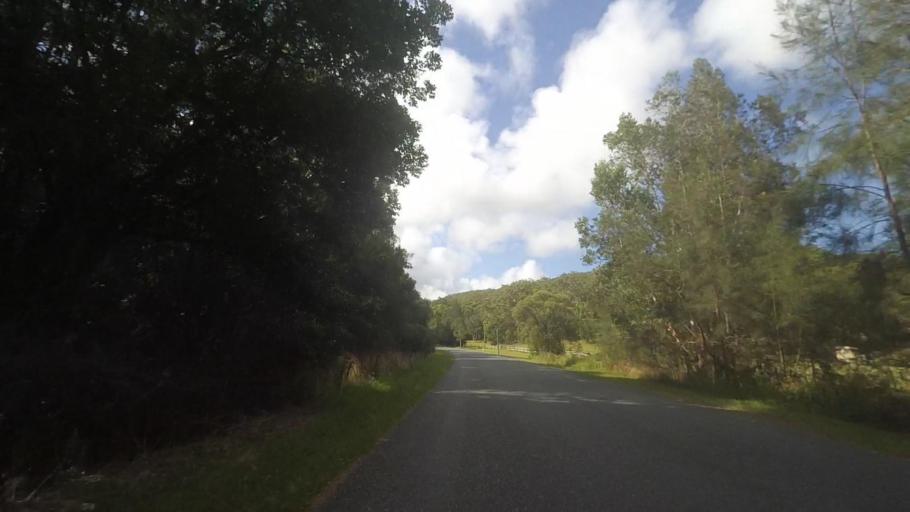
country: AU
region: New South Wales
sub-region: Great Lakes
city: Forster
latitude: -32.3992
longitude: 152.4596
